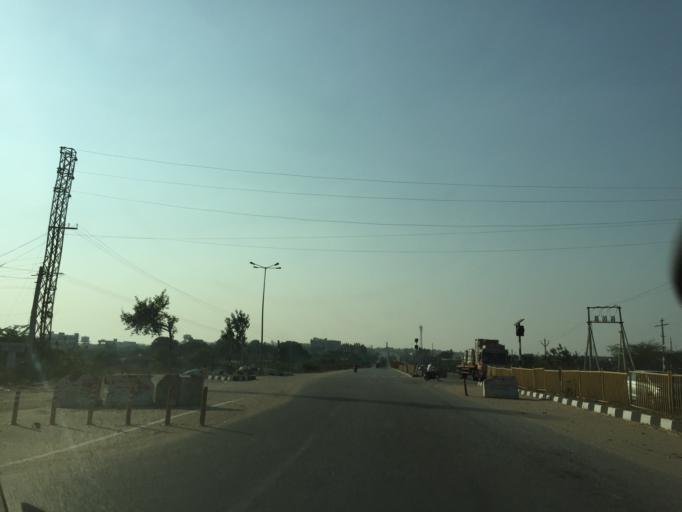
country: IN
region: Telangana
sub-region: Nalgonda
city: Bhongir
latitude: 17.5011
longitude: 78.8825
